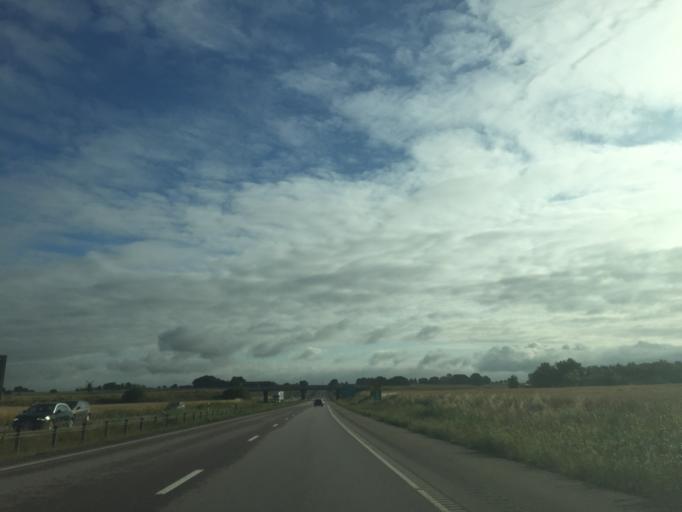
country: SE
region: Skane
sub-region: Helsingborg
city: Odakra
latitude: 56.0961
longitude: 12.7890
